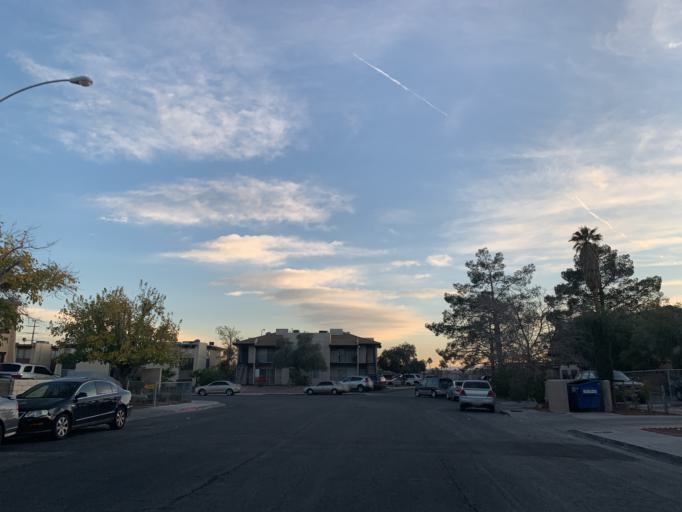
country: US
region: Nevada
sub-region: Clark County
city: Spring Valley
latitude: 36.1122
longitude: -115.2159
